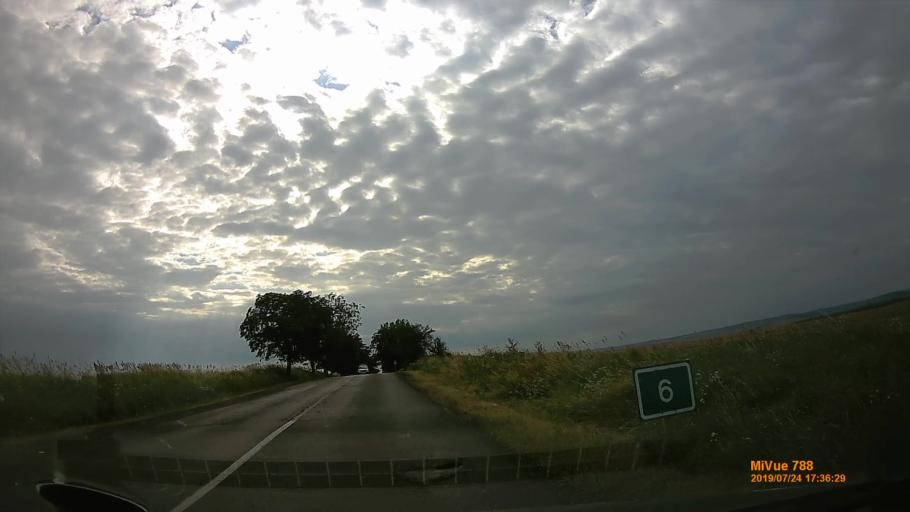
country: HU
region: Borsod-Abauj-Zemplen
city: Encs
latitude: 48.3134
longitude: 21.1702
